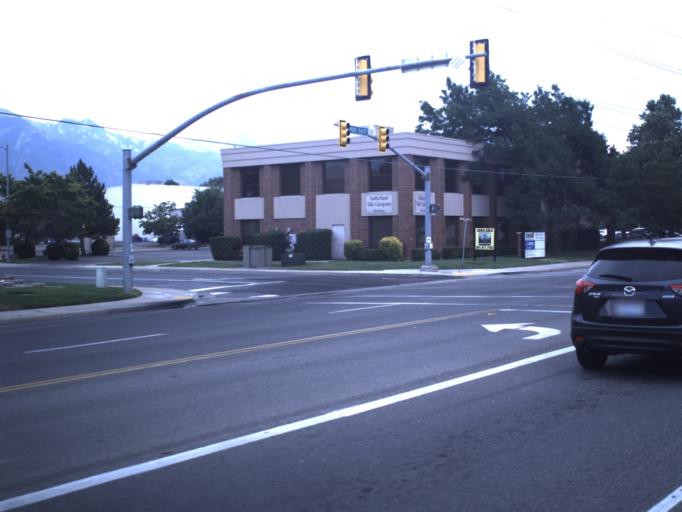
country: US
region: Utah
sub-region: Salt Lake County
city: Murray
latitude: 40.6539
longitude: -111.8660
